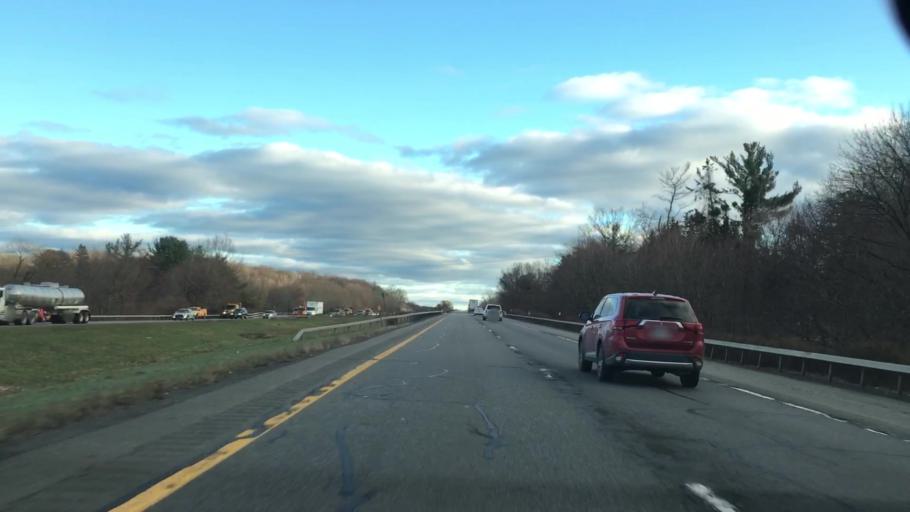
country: US
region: New York
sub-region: Putnam County
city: Brewster
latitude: 41.4119
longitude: -73.6156
